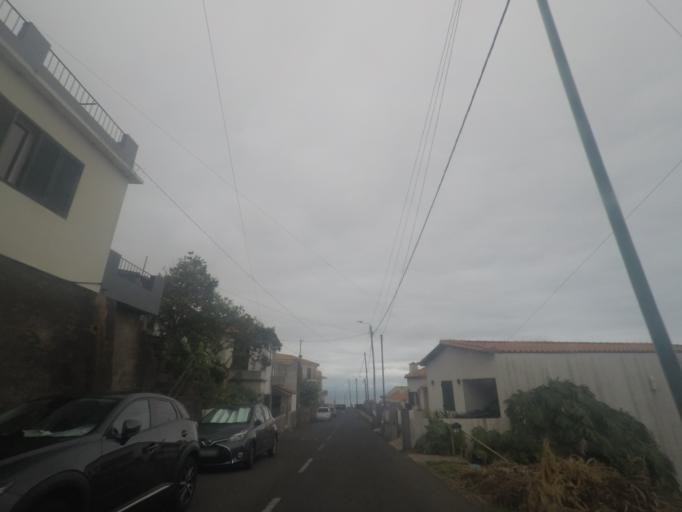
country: PT
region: Madeira
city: Camara de Lobos
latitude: 32.6666
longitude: -16.9653
